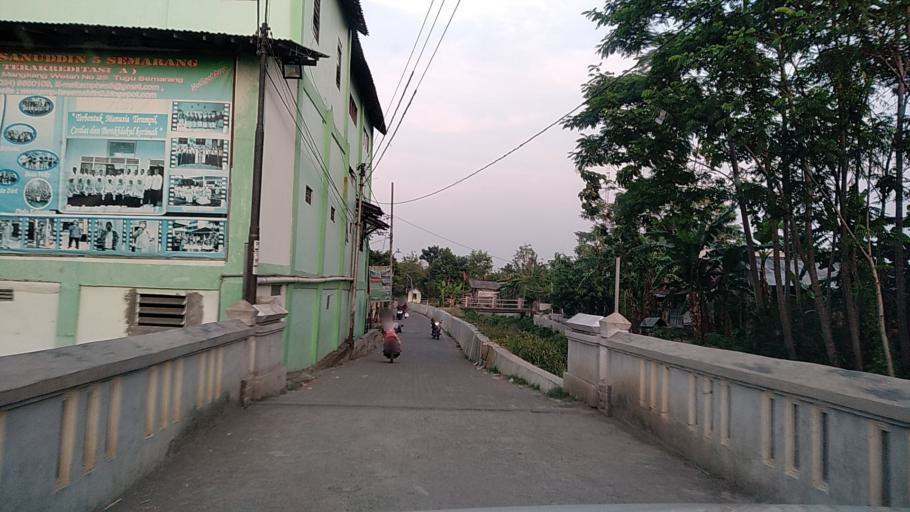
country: ID
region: Central Java
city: Semarang
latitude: -6.9711
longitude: 110.3074
